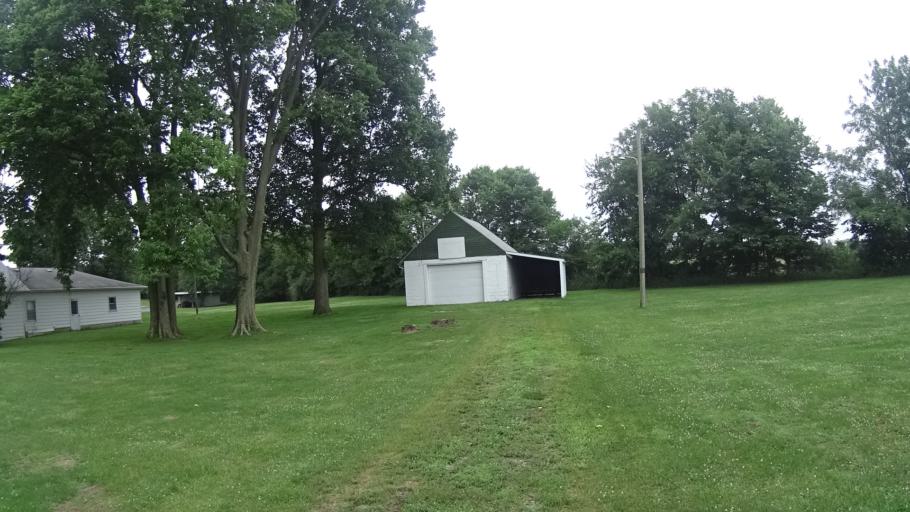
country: US
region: Indiana
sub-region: Madison County
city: Pendleton
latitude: 39.9886
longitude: -85.7442
